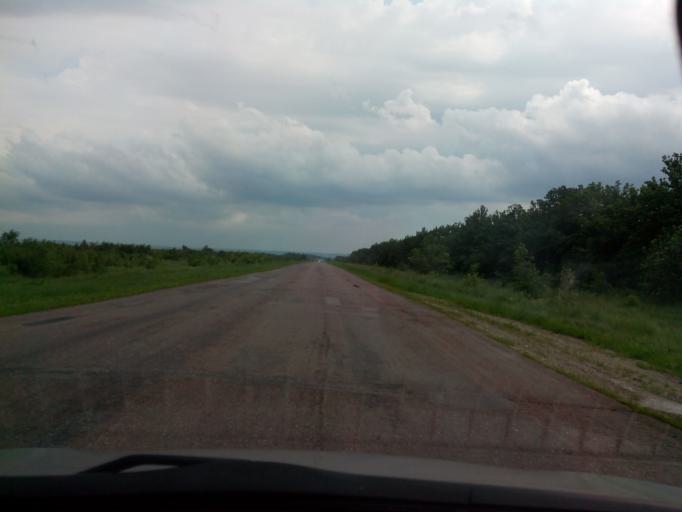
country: RU
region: Volgograd
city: Mikhaylovka
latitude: 49.9873
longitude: 43.0925
